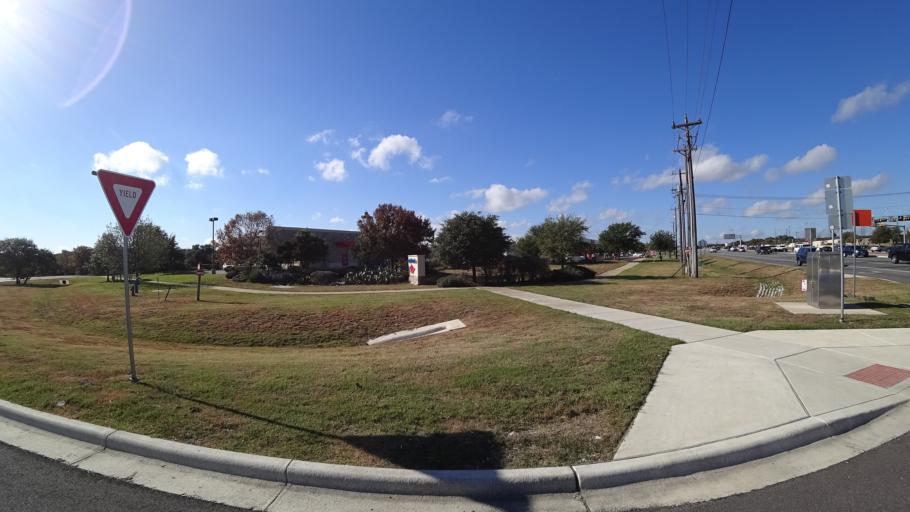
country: US
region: Texas
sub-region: Williamson County
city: Cedar Park
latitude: 30.5343
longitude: -97.7828
